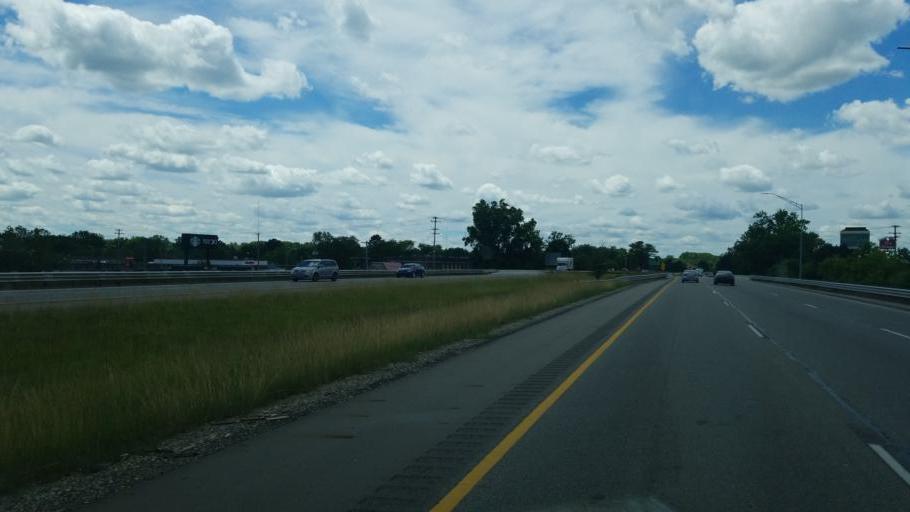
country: US
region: Michigan
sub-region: Ingham County
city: Holt
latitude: 42.6609
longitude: -84.5360
